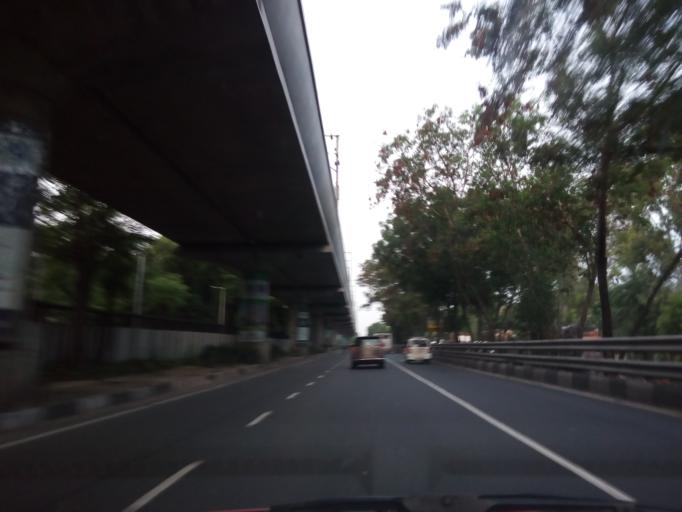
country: IN
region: NCT
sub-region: Central Delhi
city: Karol Bagh
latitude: 28.5885
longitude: 77.1527
